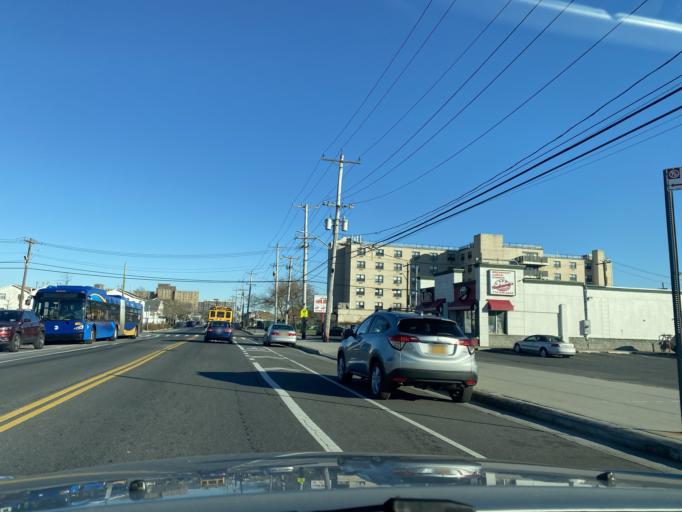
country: US
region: New York
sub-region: Nassau County
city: Inwood
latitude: 40.5953
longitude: -73.7807
